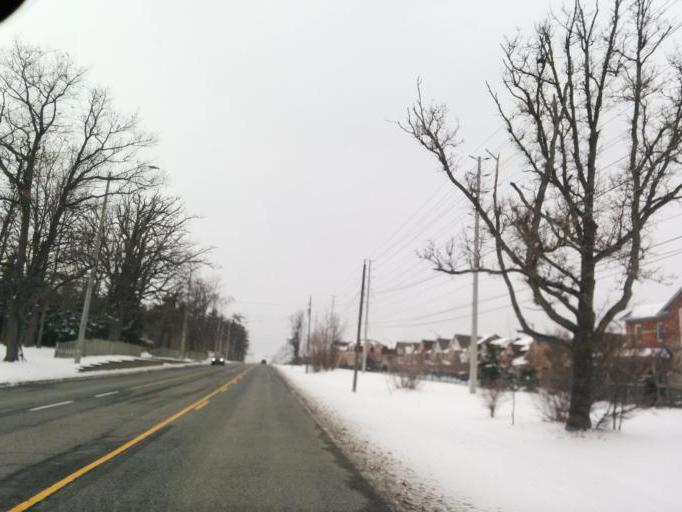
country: CA
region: Ontario
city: Mississauga
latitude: 43.5374
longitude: -79.7364
